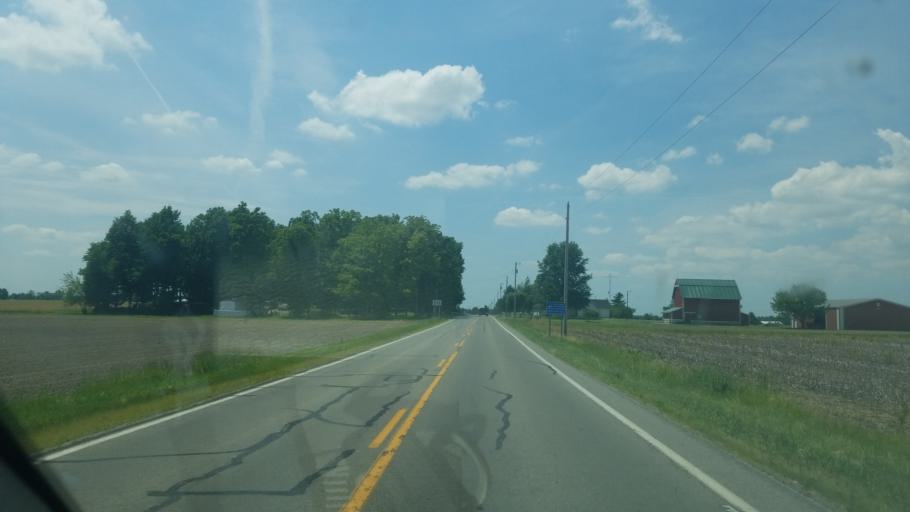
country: US
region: Ohio
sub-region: Hardin County
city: Ada
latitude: 40.7765
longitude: -83.8697
